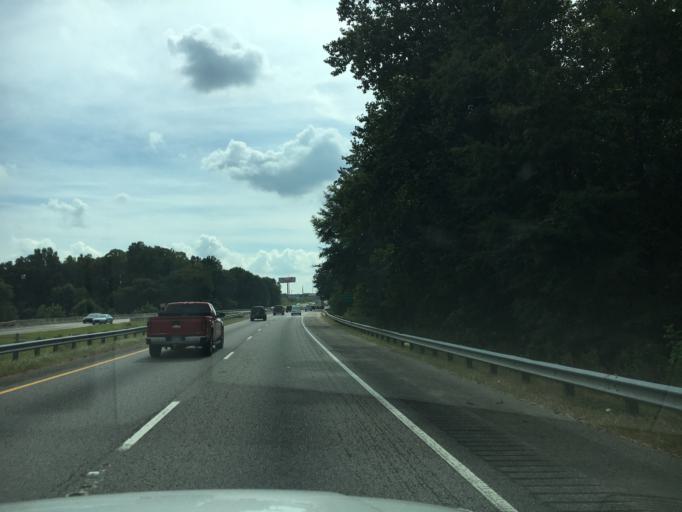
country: US
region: Georgia
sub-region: Jackson County
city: Braselton
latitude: 34.1020
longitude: -83.7921
